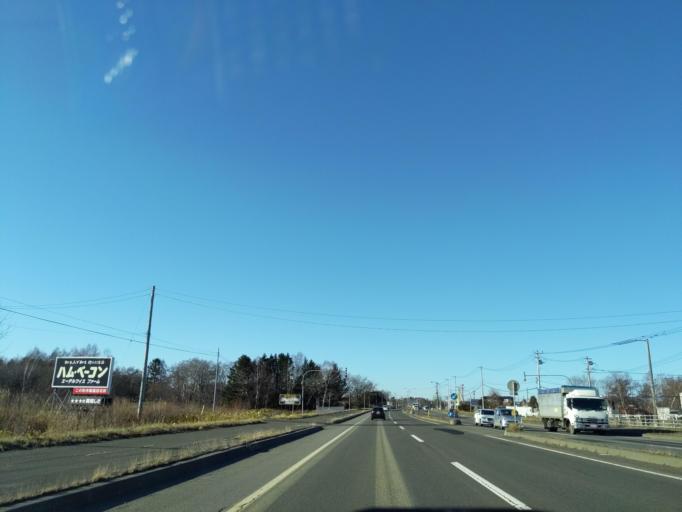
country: JP
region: Hokkaido
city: Kitahiroshima
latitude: 42.9379
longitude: 141.5101
